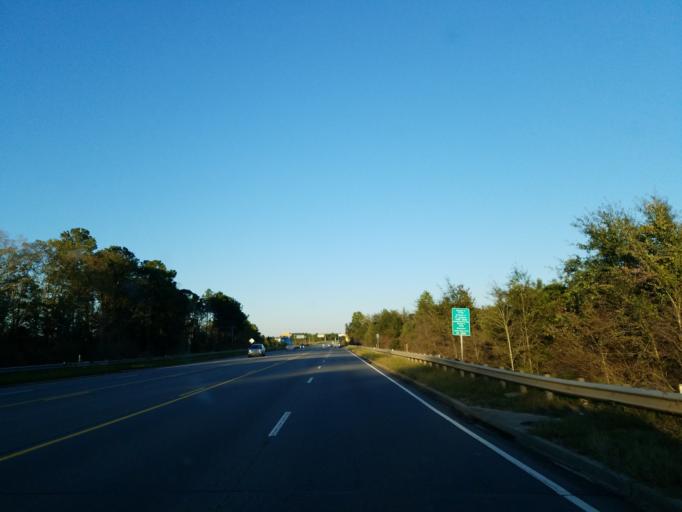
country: US
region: Georgia
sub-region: Tift County
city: Unionville
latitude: 31.4397
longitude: -83.5591
